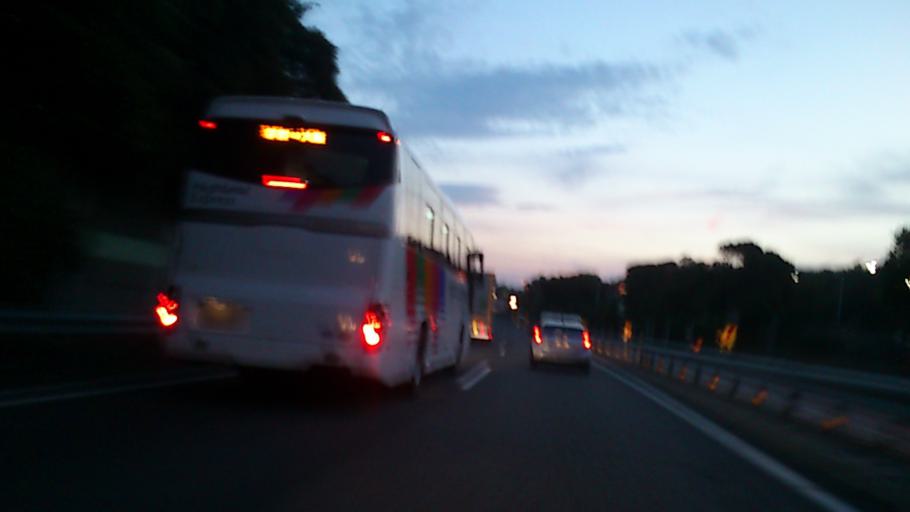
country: JP
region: Gifu
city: Tajimi
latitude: 35.3522
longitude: 137.1289
